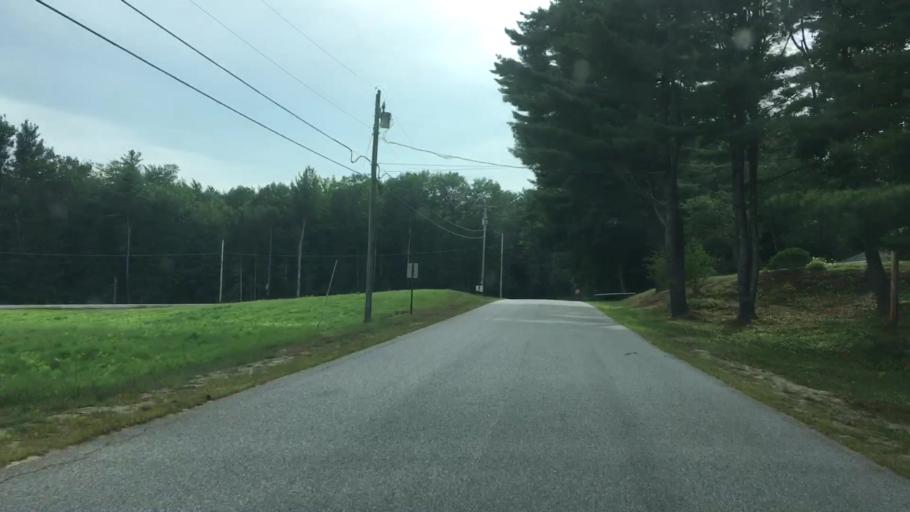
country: US
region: Maine
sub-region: Oxford County
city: Norway
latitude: 44.2251
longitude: -70.6247
